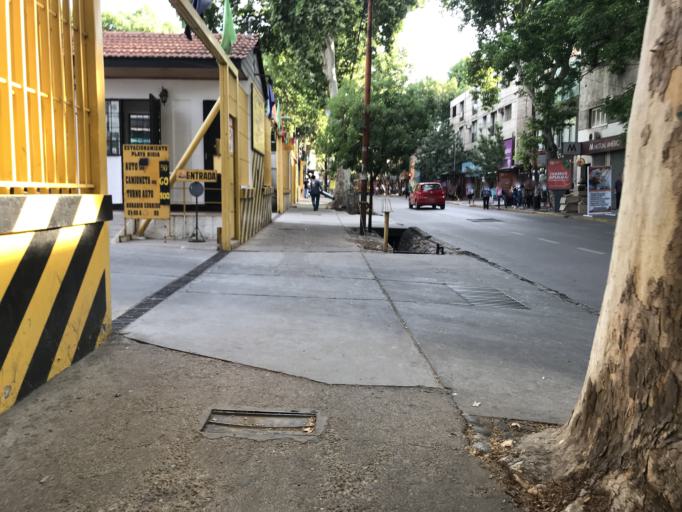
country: AR
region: Mendoza
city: Mendoza
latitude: -32.8891
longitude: -68.8355
